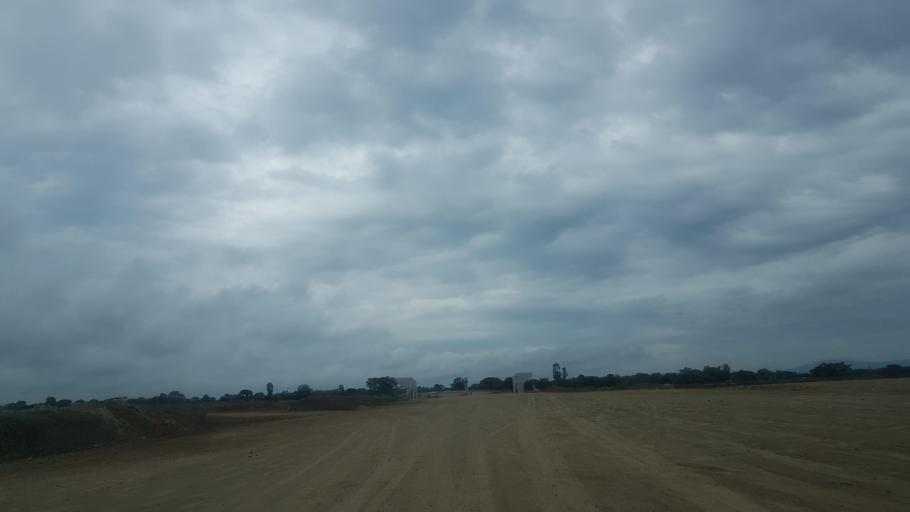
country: ET
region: Oromiya
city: Shashemene
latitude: 7.3574
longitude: 38.6408
